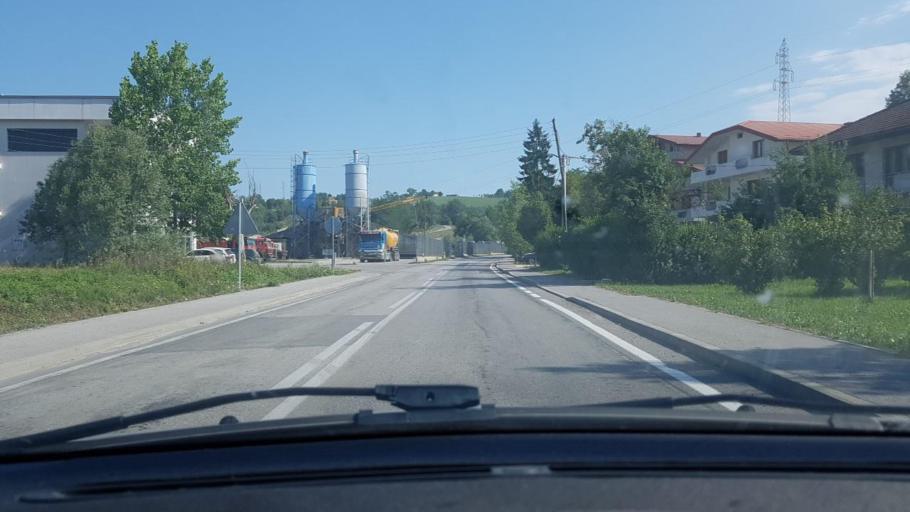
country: BA
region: Federation of Bosnia and Herzegovina
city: Coralici
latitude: 44.9925
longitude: 15.8973
